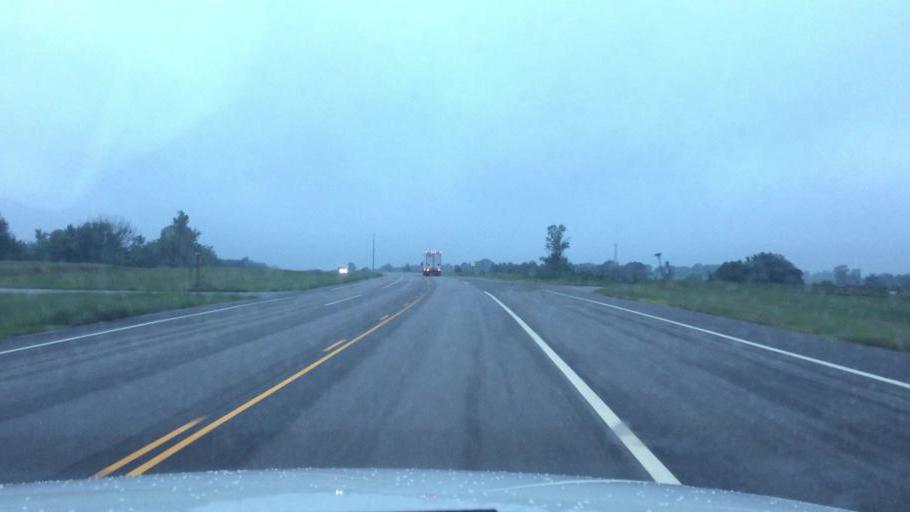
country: US
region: Kansas
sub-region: Montgomery County
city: Cherryvale
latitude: 37.4571
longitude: -95.4819
